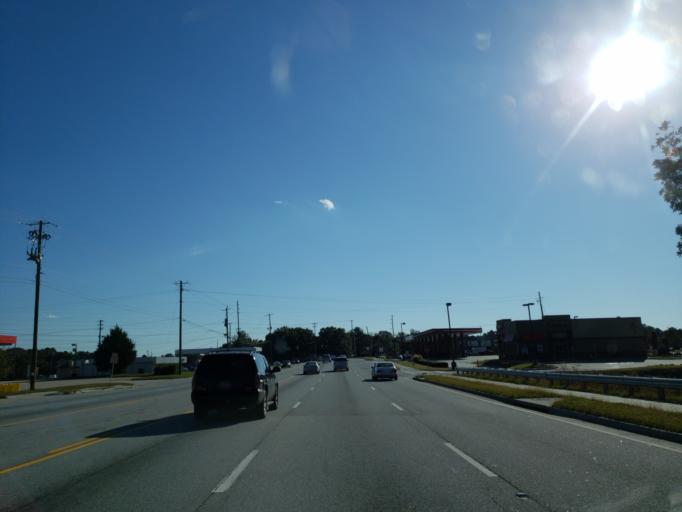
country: US
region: Georgia
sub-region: Gwinnett County
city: Lawrenceville
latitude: 33.9764
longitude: -83.9862
